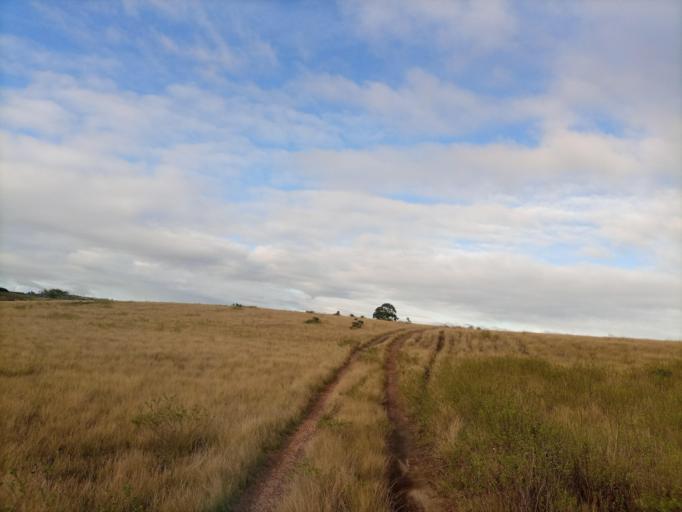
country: MG
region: Anosy
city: Fort Dauphin
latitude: -24.3128
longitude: 47.2603
